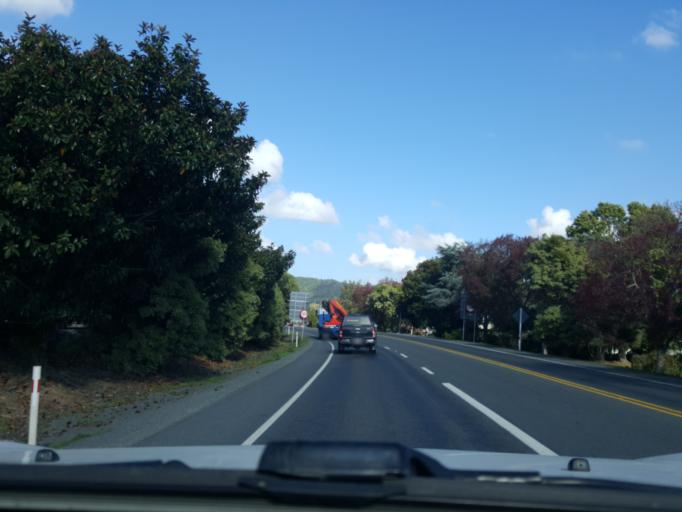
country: NZ
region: Waikato
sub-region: Waikato District
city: Ngaruawahia
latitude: -37.5801
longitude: 175.1593
